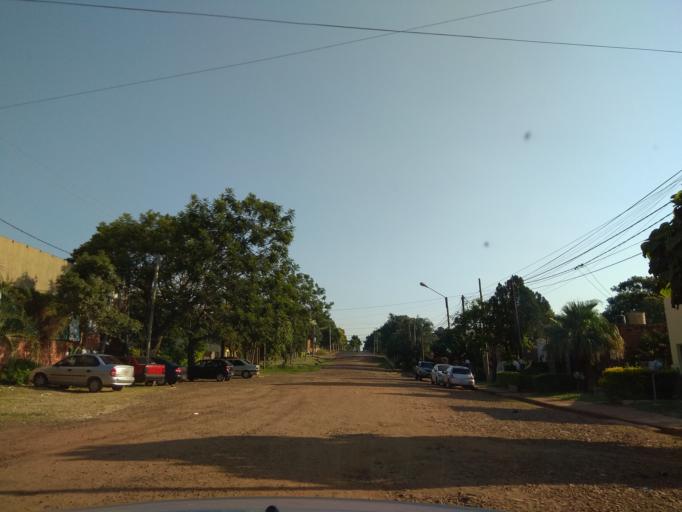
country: AR
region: Misiones
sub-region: Departamento de Capital
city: Posadas
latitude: -27.3628
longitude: -55.9273
